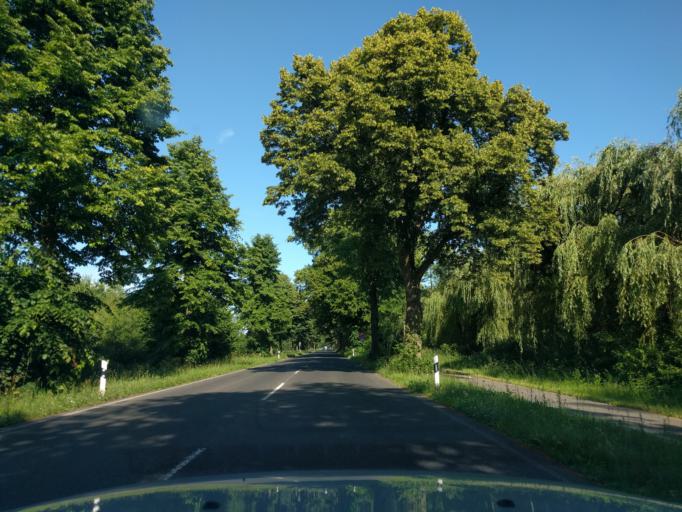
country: DE
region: North Rhine-Westphalia
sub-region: Regierungsbezirk Dusseldorf
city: Willich
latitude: 51.2284
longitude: 6.5697
